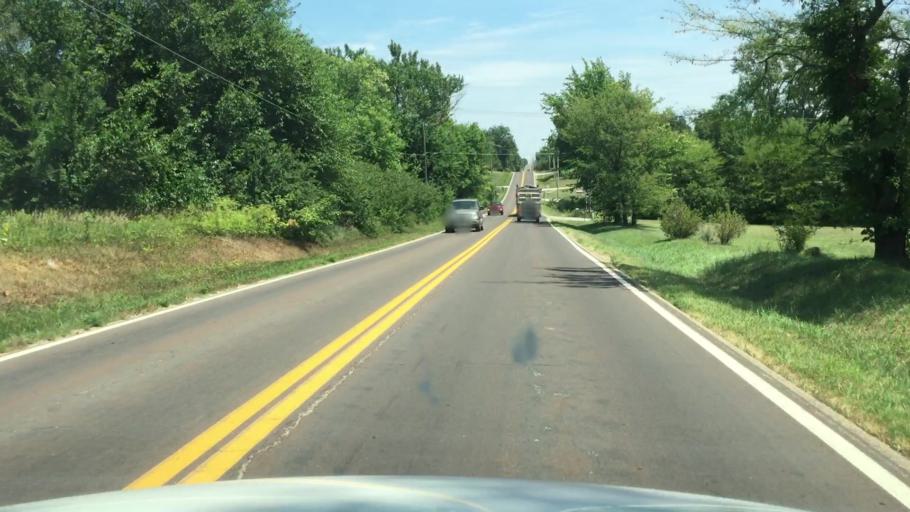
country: US
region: Kansas
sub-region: Shawnee County
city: Topeka
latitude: 38.9861
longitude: -95.5670
